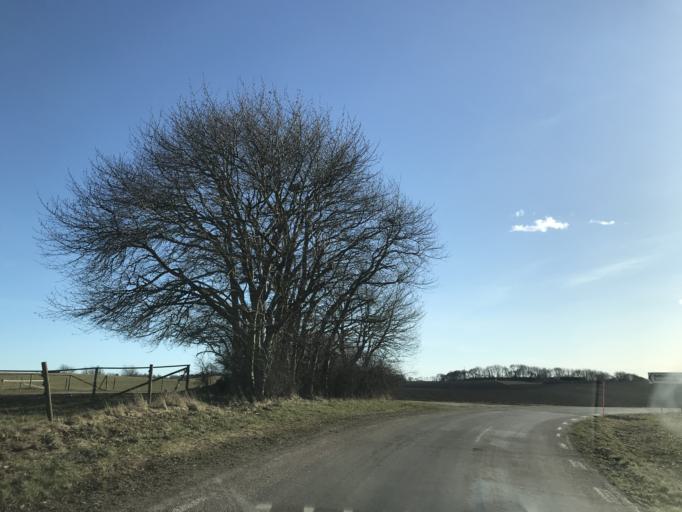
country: SE
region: Skane
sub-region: Ystads Kommun
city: Ystad
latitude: 55.5345
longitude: 13.7843
